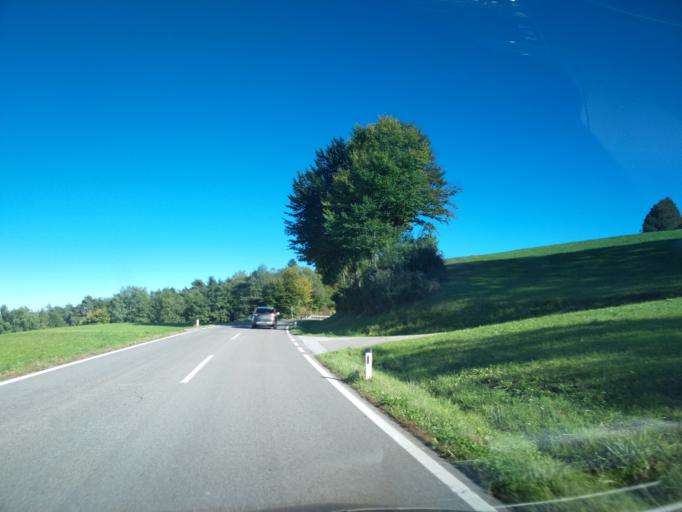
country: AT
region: Styria
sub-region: Politischer Bezirk Voitsberg
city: Ligist
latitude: 46.9784
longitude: 15.2143
